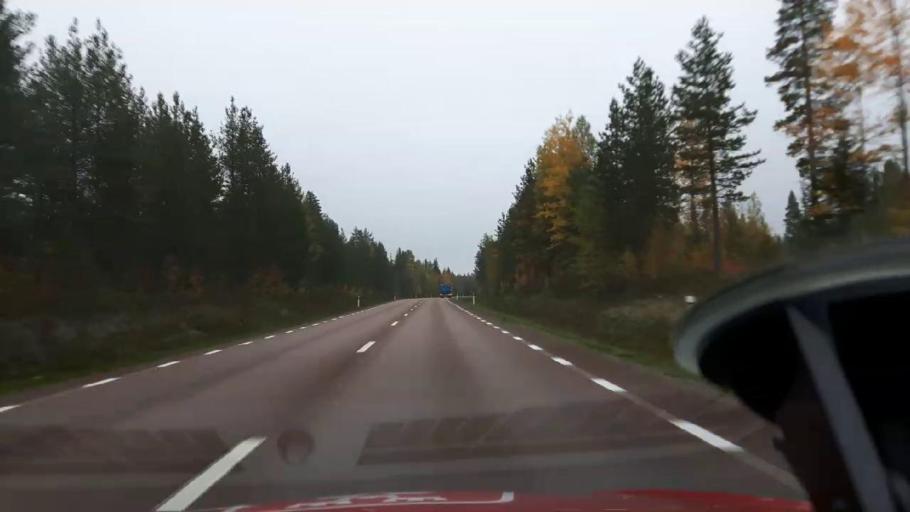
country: SE
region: Jaemtland
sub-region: Bergs Kommun
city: Hoverberg
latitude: 62.6025
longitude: 14.4123
